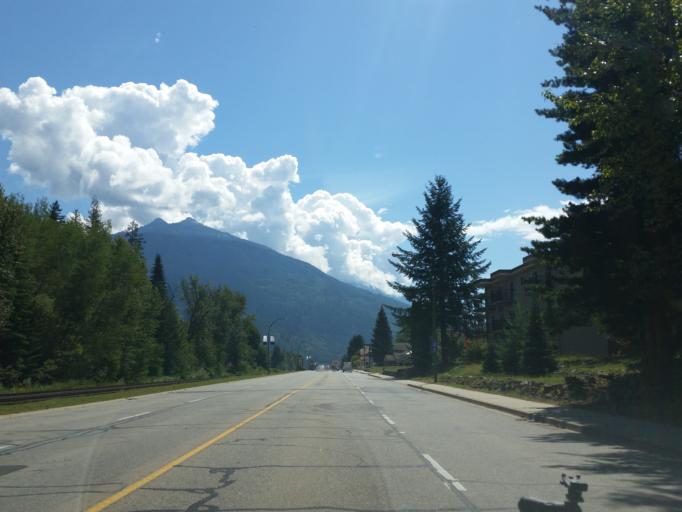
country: CA
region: British Columbia
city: Revelstoke
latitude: 51.0073
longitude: -118.2073
